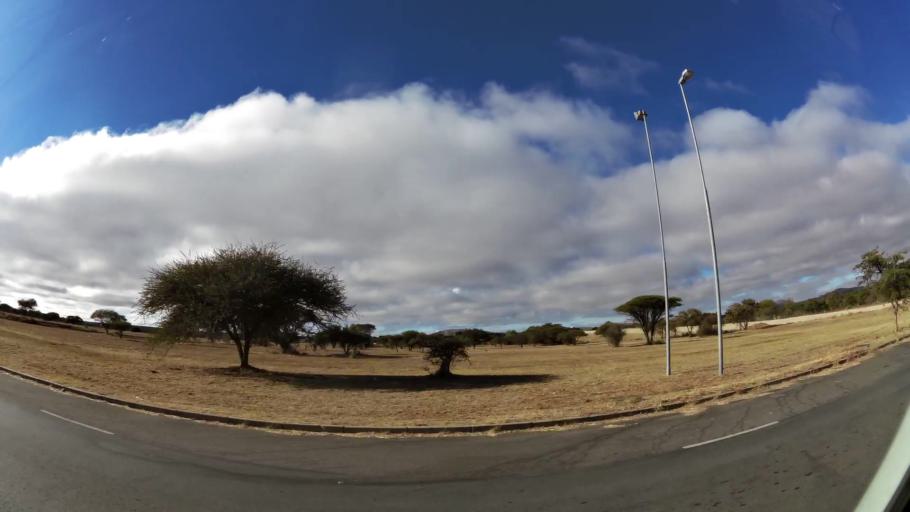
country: ZA
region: Limpopo
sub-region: Capricorn District Municipality
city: Polokwane
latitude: -23.9280
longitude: 29.4674
